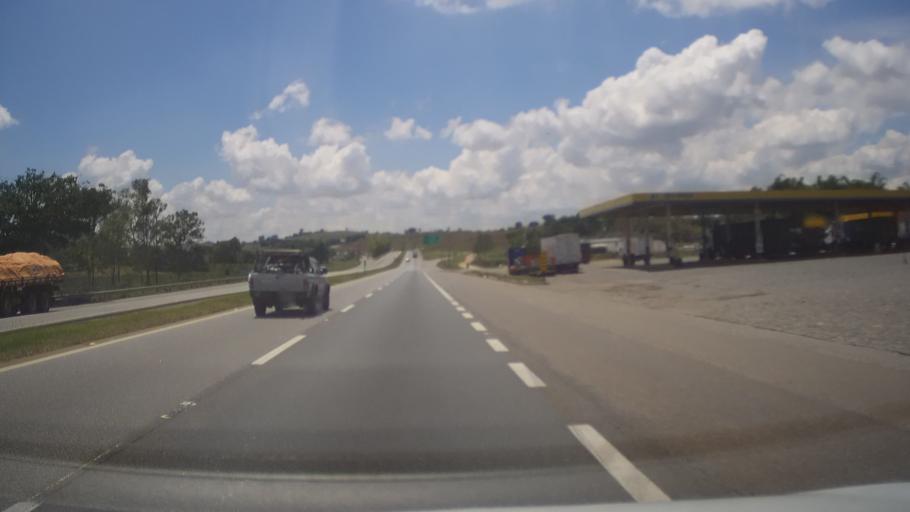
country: BR
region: Minas Gerais
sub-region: Sao Goncalo Do Sapucai
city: Sao Goncalo do Sapucai
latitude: -21.9159
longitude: -45.5844
